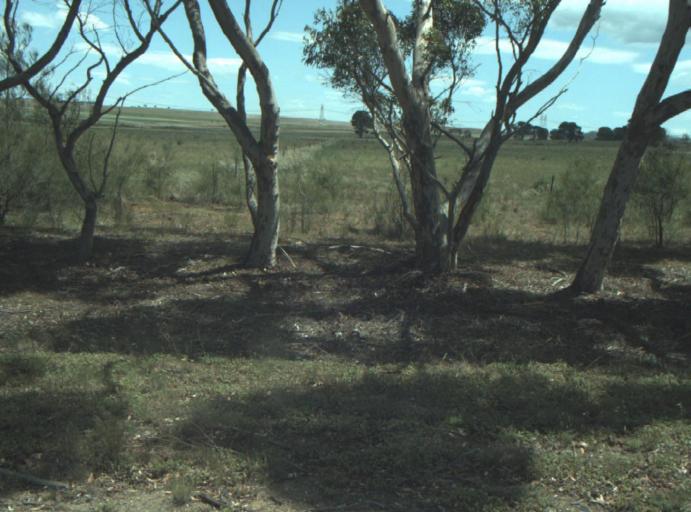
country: AU
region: Victoria
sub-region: Greater Geelong
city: Lara
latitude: -37.9638
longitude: 144.3506
